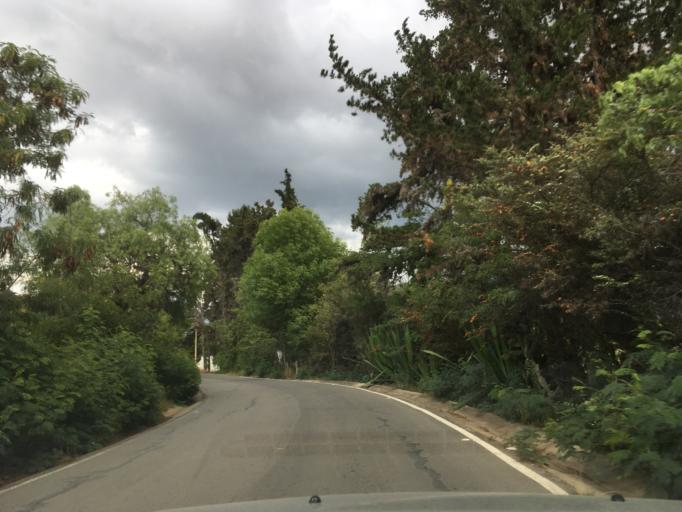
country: CO
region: Boyaca
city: Villa de Leiva
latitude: 5.6268
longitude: -73.5634
